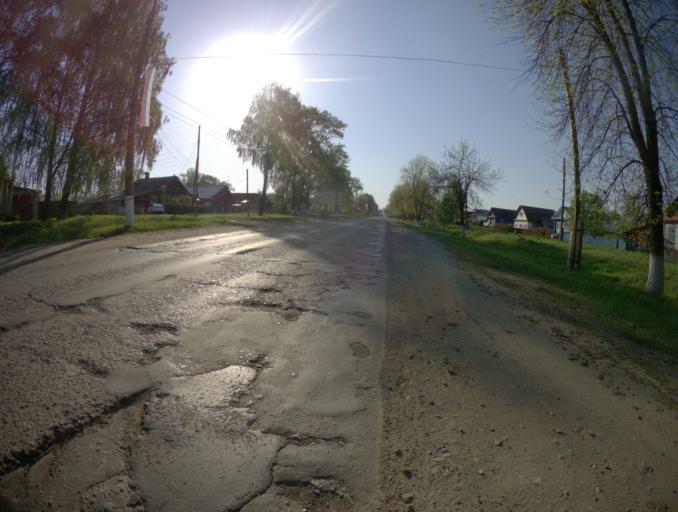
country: RU
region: Vladimir
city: Vyazniki
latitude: 56.2368
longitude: 42.1797
